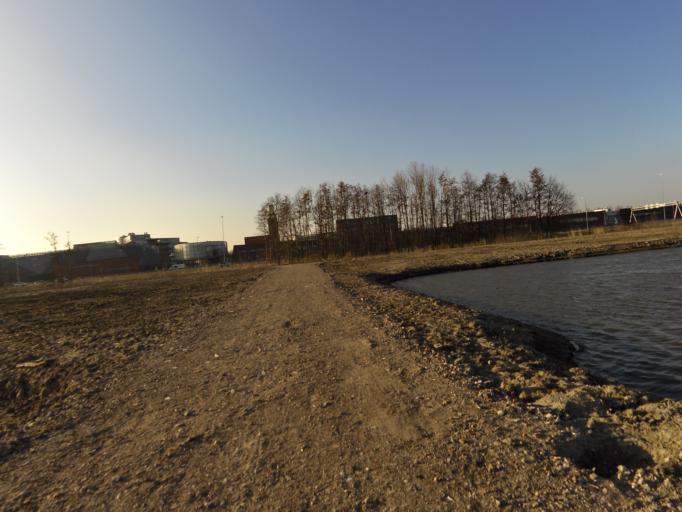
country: NL
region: South Holland
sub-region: Gemeente Leiderdorp
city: Leiderdorp
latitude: 52.1551
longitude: 4.5468
